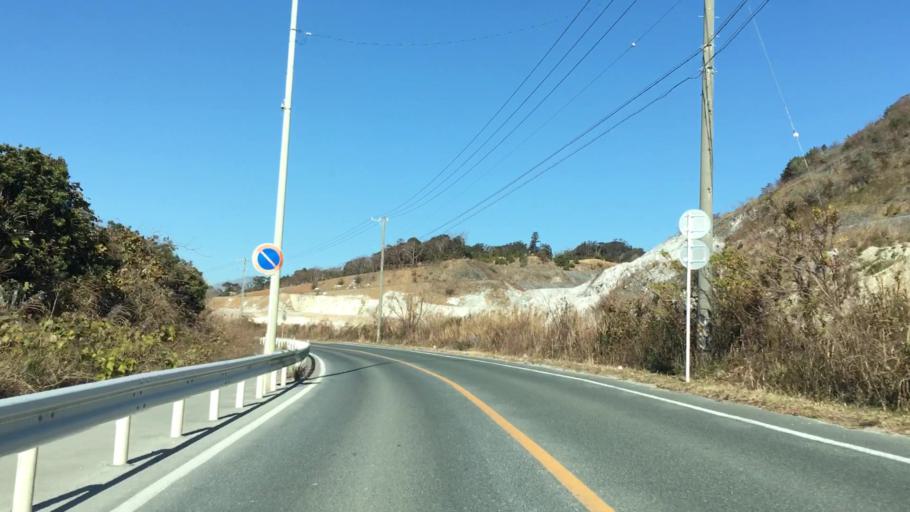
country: JP
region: Aichi
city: Tahara
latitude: 34.6816
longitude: 137.2515
